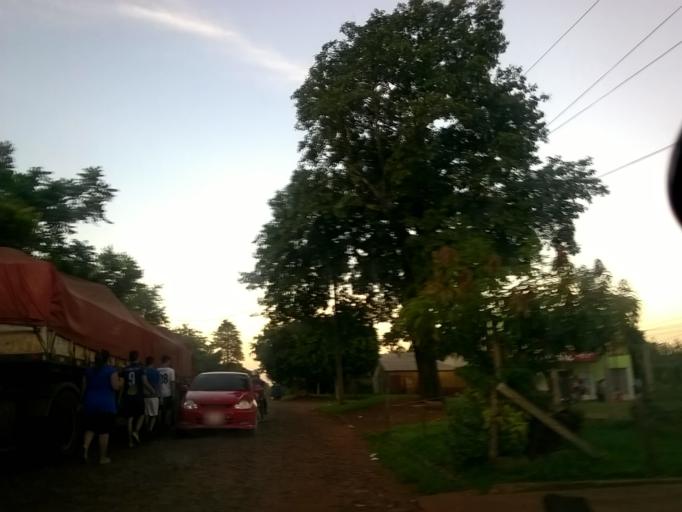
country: PY
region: Alto Parana
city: Ciudad del Este
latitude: -25.4796
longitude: -54.6459
